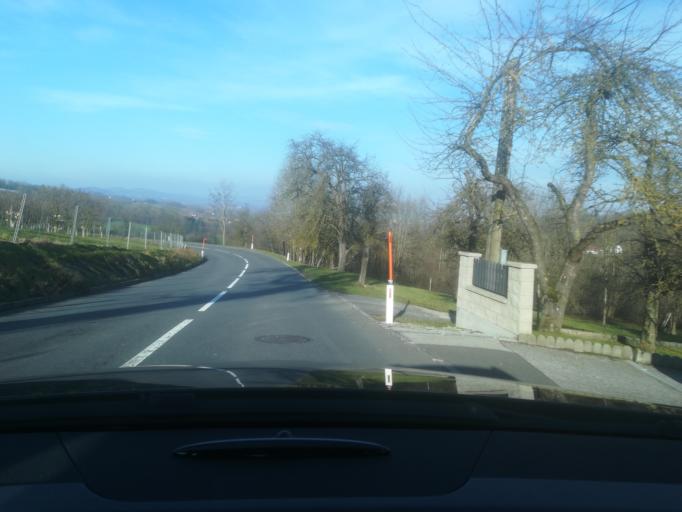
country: AT
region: Upper Austria
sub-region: Wels-Land
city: Buchkirchen
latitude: 48.2554
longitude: 14.0382
